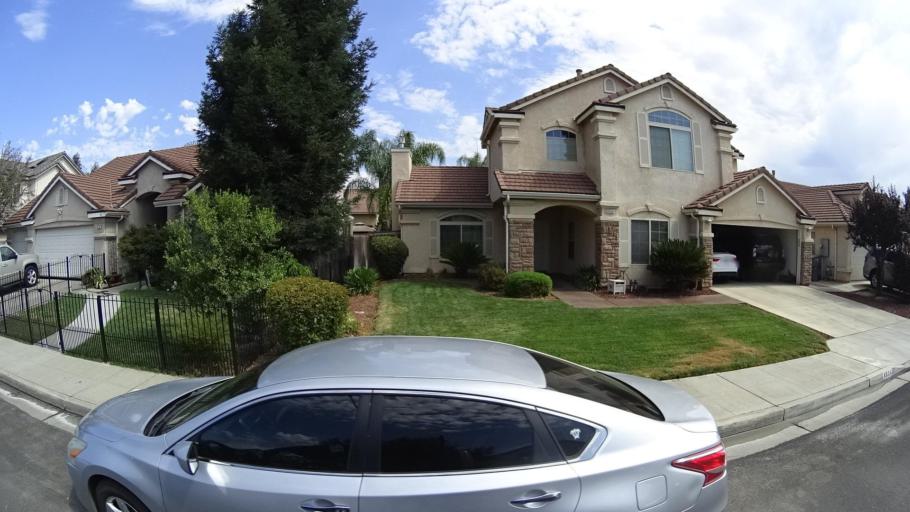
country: US
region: California
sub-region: Fresno County
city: Tarpey Village
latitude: 36.7781
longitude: -119.6710
